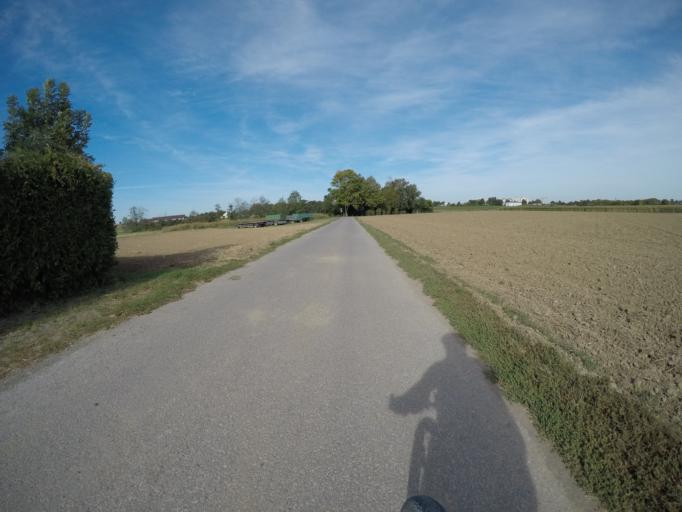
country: DE
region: Baden-Wuerttemberg
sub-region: Regierungsbezirk Stuttgart
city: Korntal
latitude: 48.8462
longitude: 9.1035
